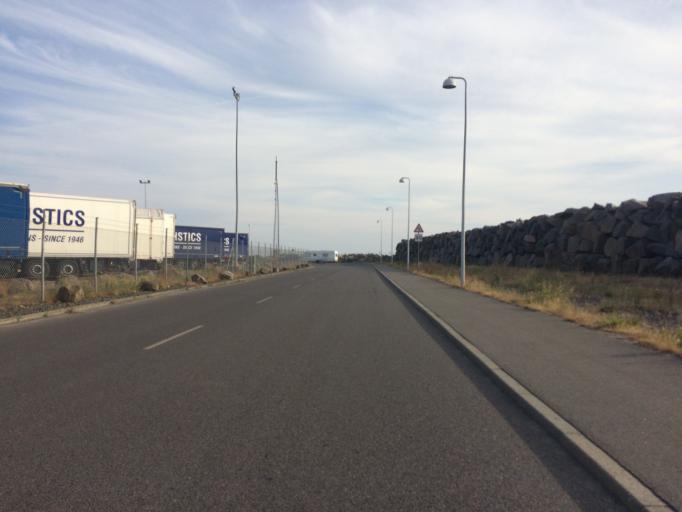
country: DK
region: Capital Region
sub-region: Bornholm Kommune
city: Ronne
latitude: 55.1021
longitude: 14.6855
